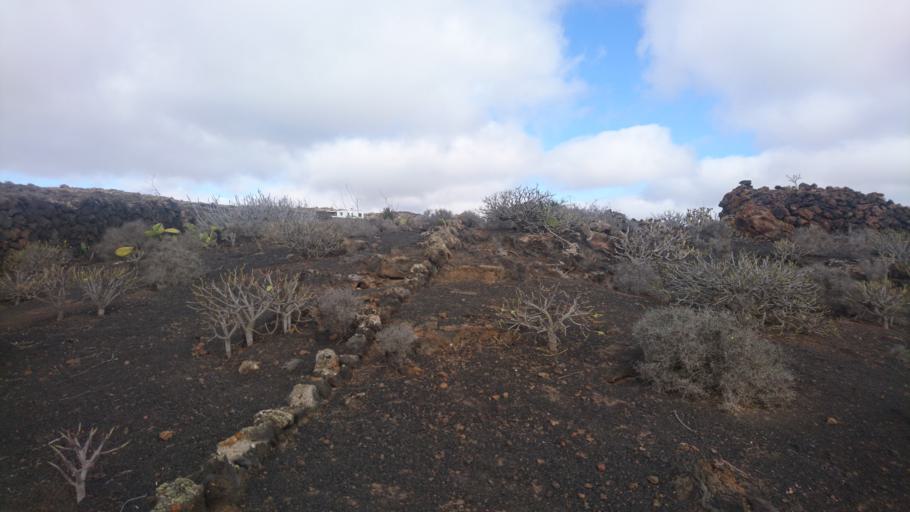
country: ES
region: Canary Islands
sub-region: Provincia de Las Palmas
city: Haria
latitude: 29.1757
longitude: -13.4652
